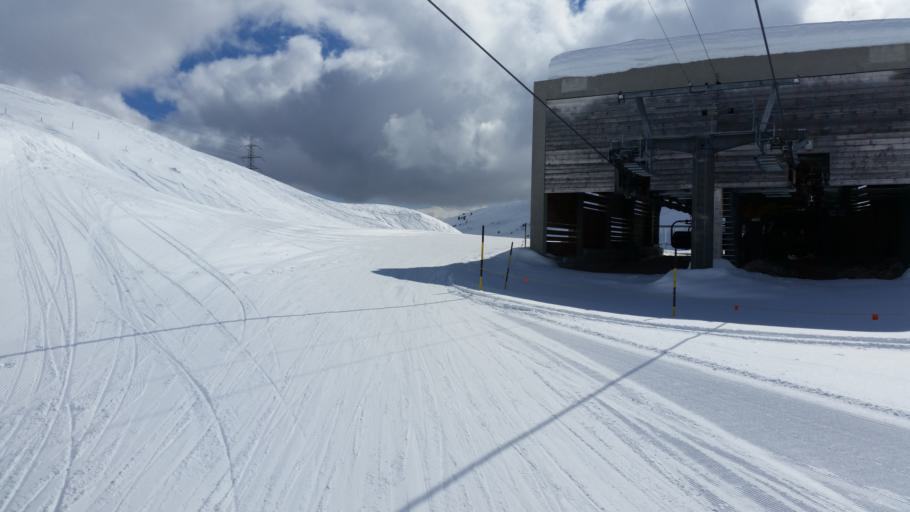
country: CH
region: Grisons
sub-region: Surselva District
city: Ilanz
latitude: 46.8432
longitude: 9.1563
